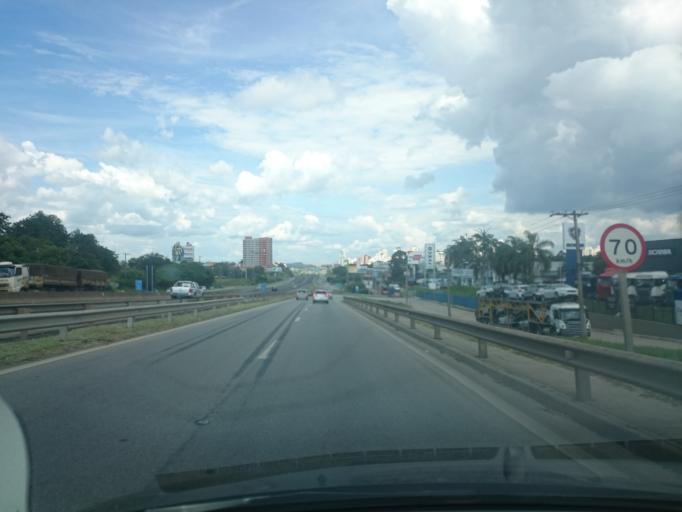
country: BR
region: Sao Paulo
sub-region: Sorocaba
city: Sorocaba
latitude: -23.5333
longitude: -47.4834
